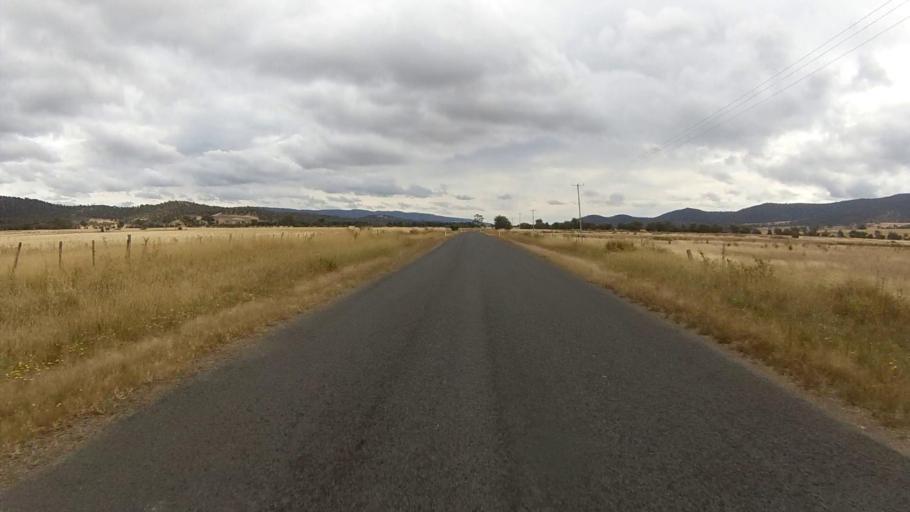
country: AU
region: Tasmania
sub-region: Break O'Day
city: St Helens
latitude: -41.8246
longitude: 147.8515
